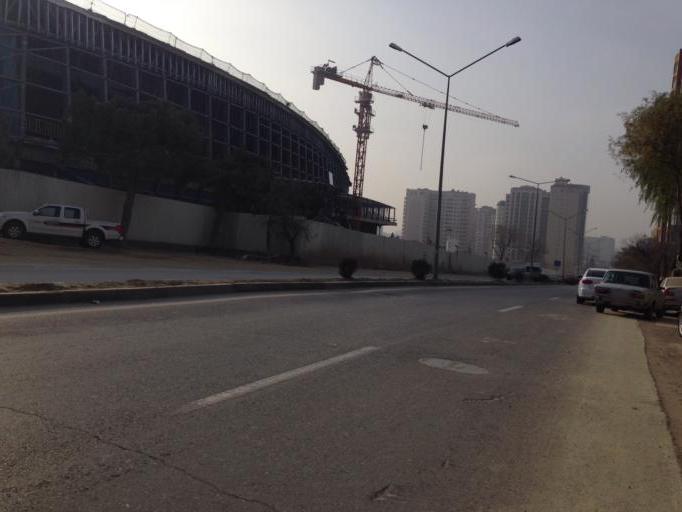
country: AZ
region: Baki
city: Baku
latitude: 40.3989
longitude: 49.8651
